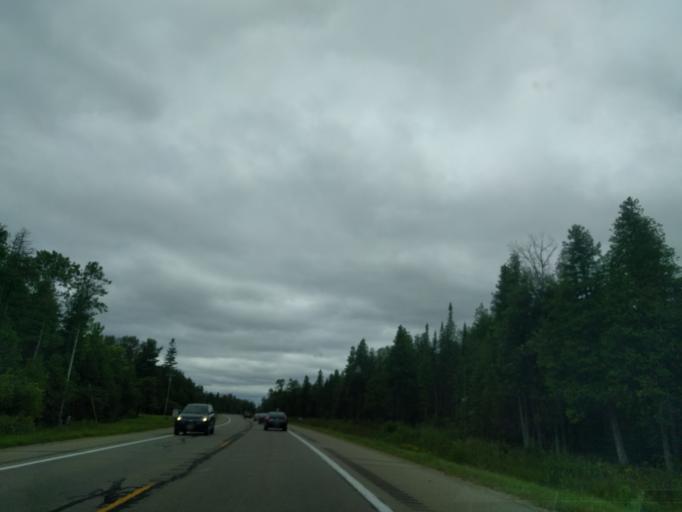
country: US
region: Michigan
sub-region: Delta County
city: Escanaba
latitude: 45.6480
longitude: -87.1860
